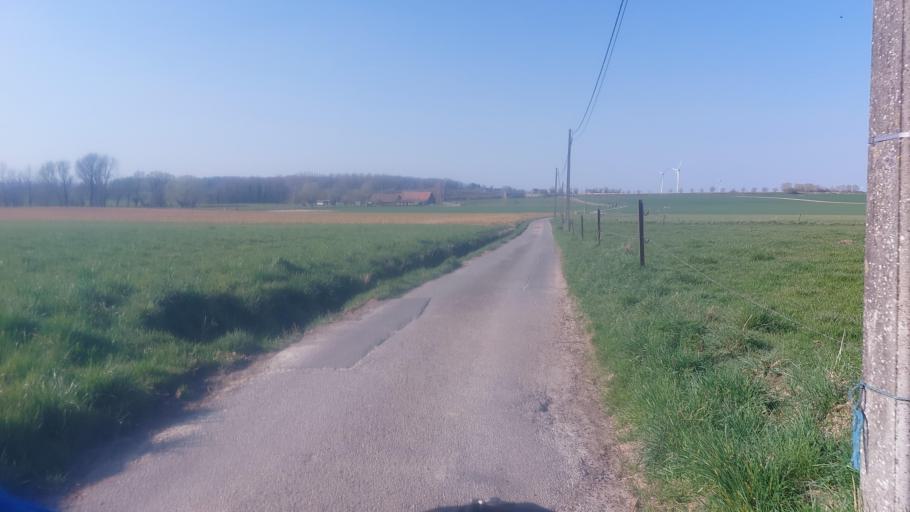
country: BE
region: Wallonia
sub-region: Province du Hainaut
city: Brugelette
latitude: 50.6304
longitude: 3.8722
